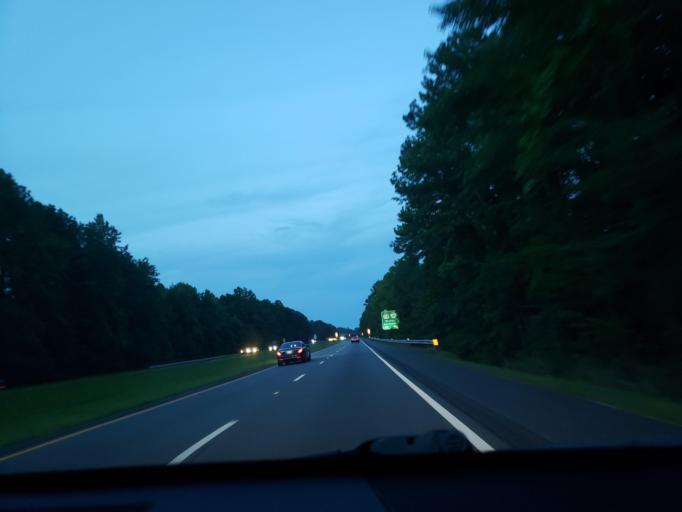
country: US
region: Virginia
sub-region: City of Franklin
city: Franklin
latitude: 36.6438
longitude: -76.8816
